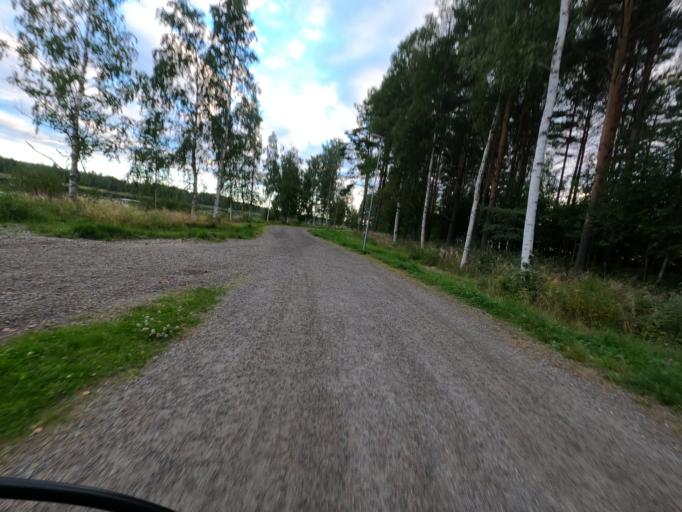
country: FI
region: North Karelia
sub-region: Joensuu
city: Joensuu
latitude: 62.6120
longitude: 29.8431
